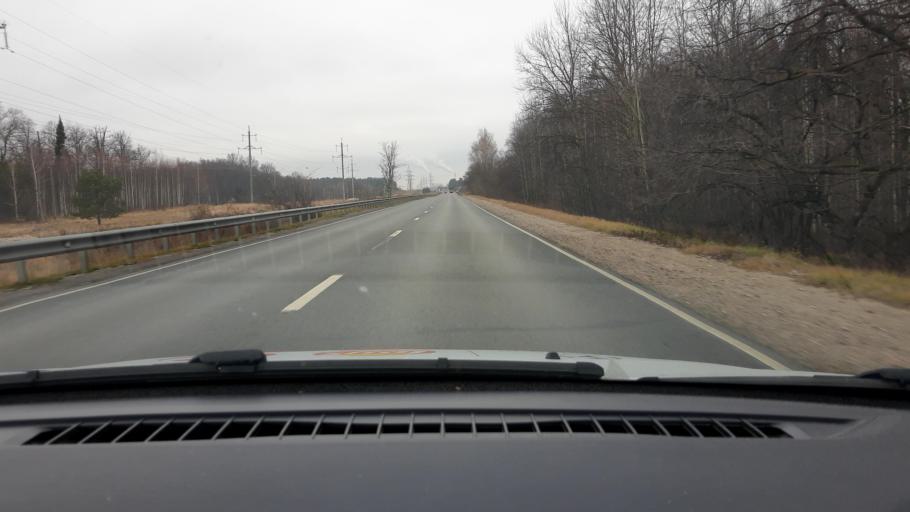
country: RU
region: Nizjnij Novgorod
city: Lukino
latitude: 56.4624
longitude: 43.6208
